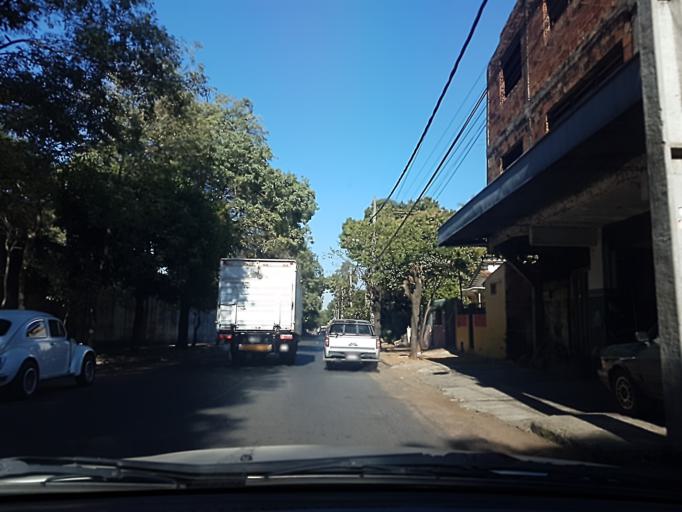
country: PY
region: Central
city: Lambare
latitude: -25.3167
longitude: -57.5885
